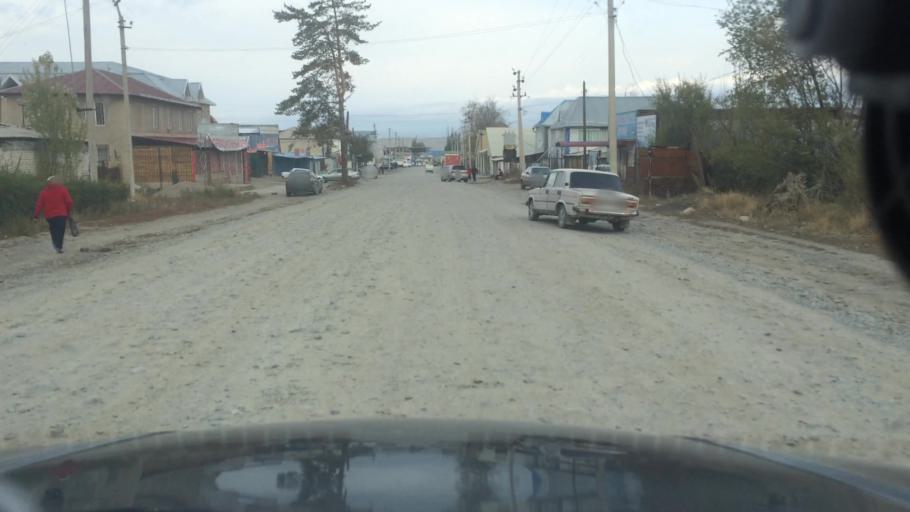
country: KG
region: Ysyk-Koel
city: Karakol
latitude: 42.4901
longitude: 78.3881
